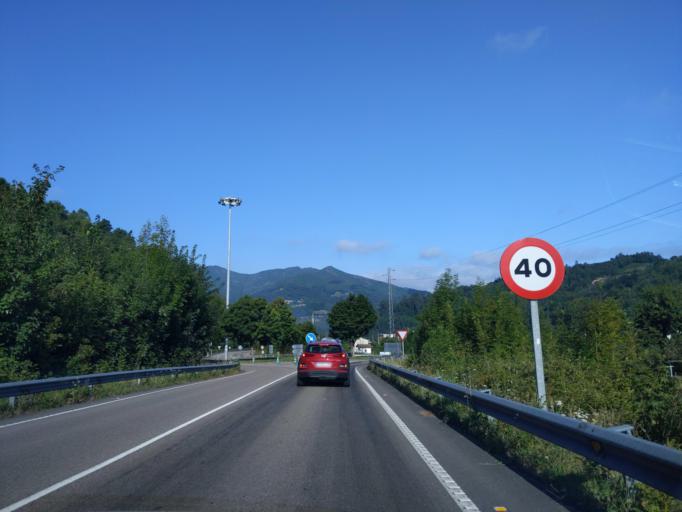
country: ES
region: Asturias
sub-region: Province of Asturias
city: Pola de Laviana
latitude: 43.2353
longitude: -5.5395
